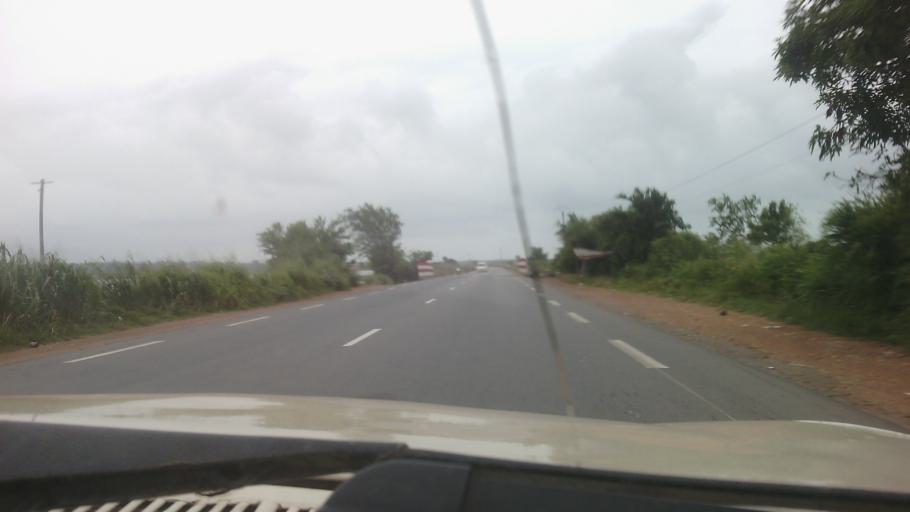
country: BJ
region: Mono
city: Come
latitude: 6.3967
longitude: 1.9269
